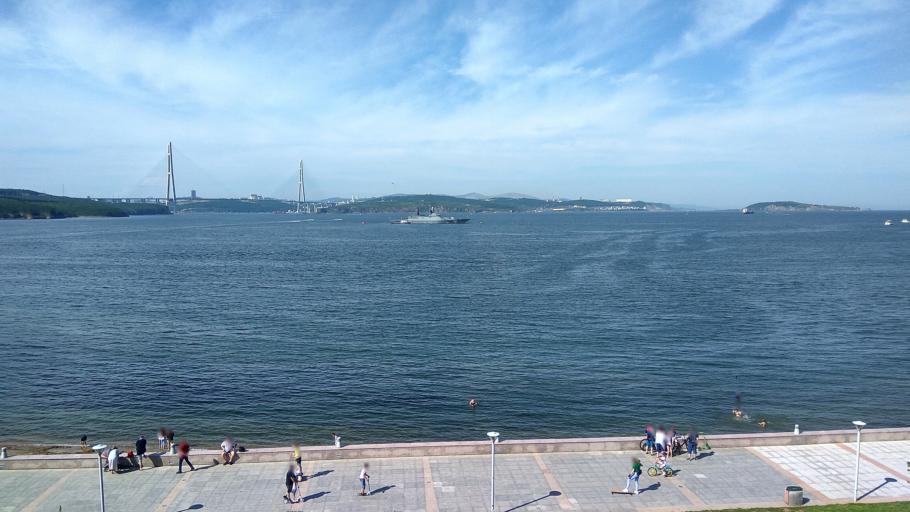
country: RU
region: Primorskiy
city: Russkiy
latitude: 43.0291
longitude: 131.8969
